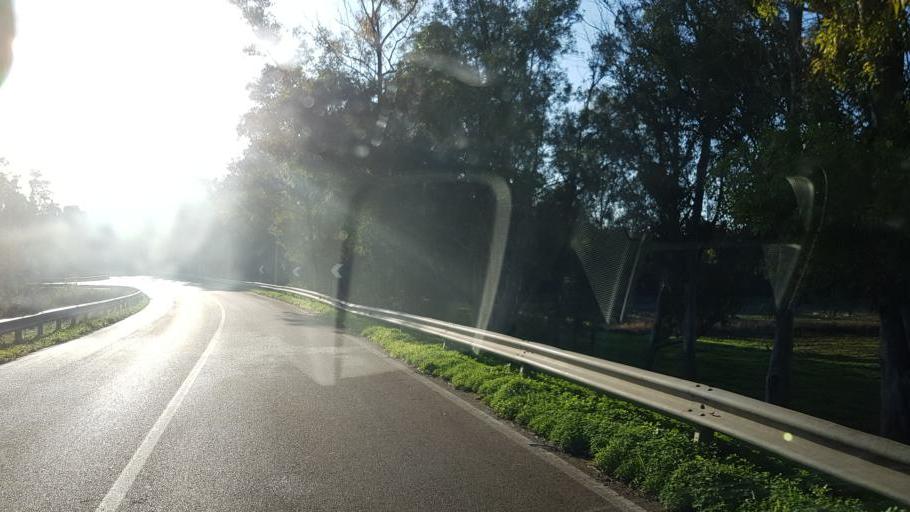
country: IT
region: Apulia
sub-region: Provincia di Brindisi
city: Torchiarolo
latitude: 40.5512
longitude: 18.0351
